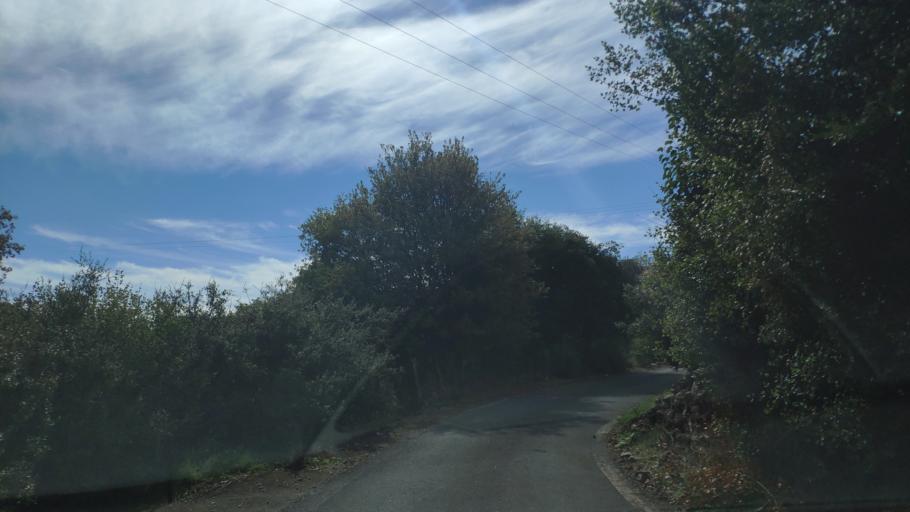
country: GR
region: Peloponnese
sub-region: Nomos Arkadias
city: Dimitsana
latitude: 37.5232
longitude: 22.0714
